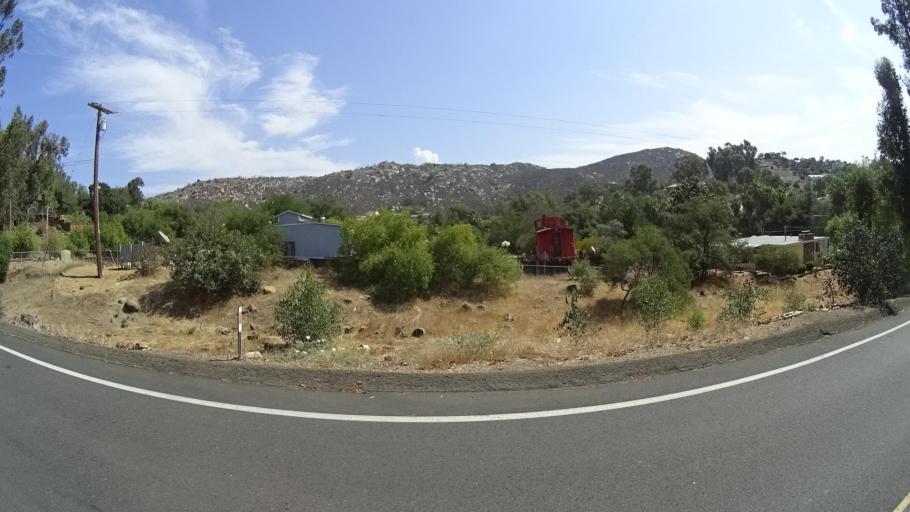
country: US
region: California
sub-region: San Diego County
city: Hidden Meadows
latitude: 33.1876
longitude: -117.1169
